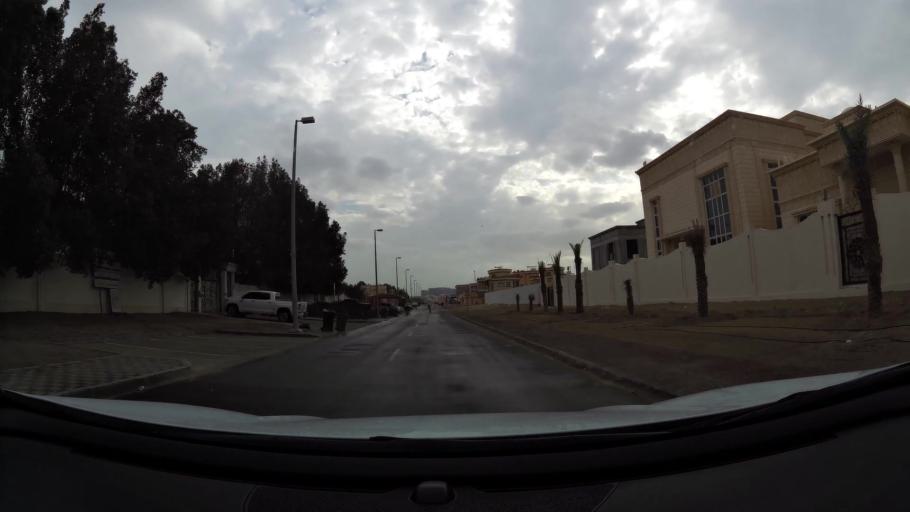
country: AE
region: Abu Dhabi
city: Abu Dhabi
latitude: 24.3437
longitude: 54.6299
